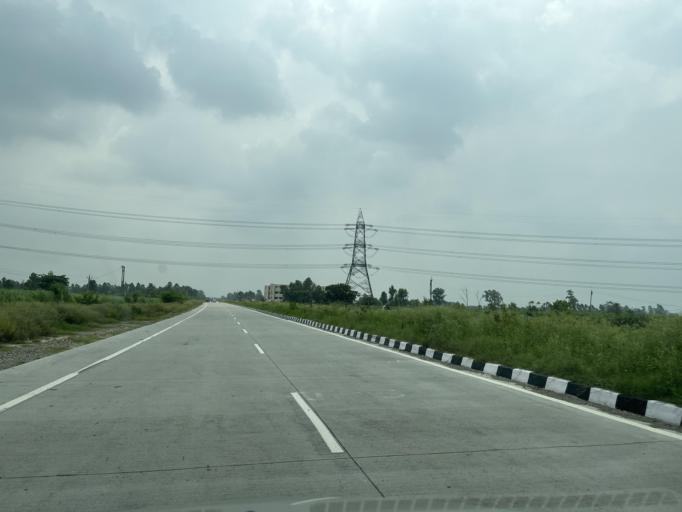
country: IN
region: Uttar Pradesh
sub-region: Bijnor
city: Najibabad
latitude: 29.5648
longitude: 78.3388
